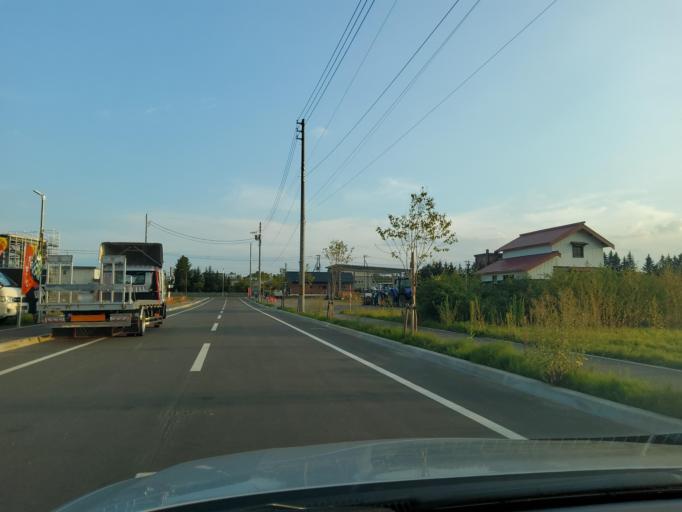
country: JP
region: Hokkaido
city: Obihiro
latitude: 42.9348
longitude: 143.1534
